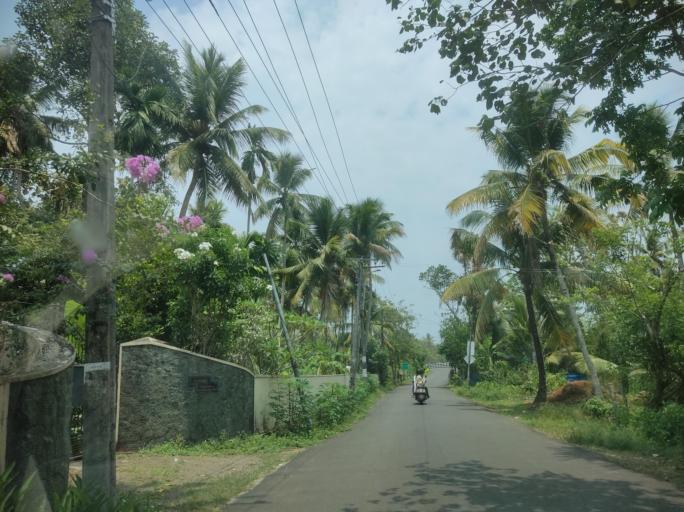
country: IN
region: Kerala
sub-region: Alappuzha
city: Vayalar
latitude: 9.7389
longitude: 76.3255
